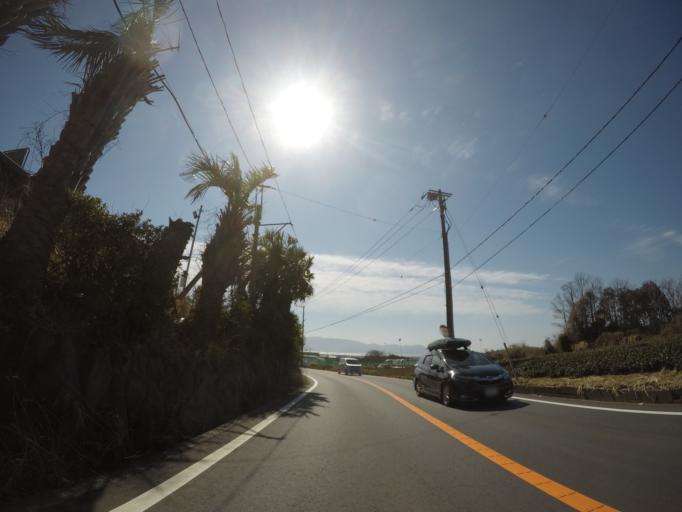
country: JP
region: Shizuoka
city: Numazu
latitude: 35.1346
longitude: 138.8359
